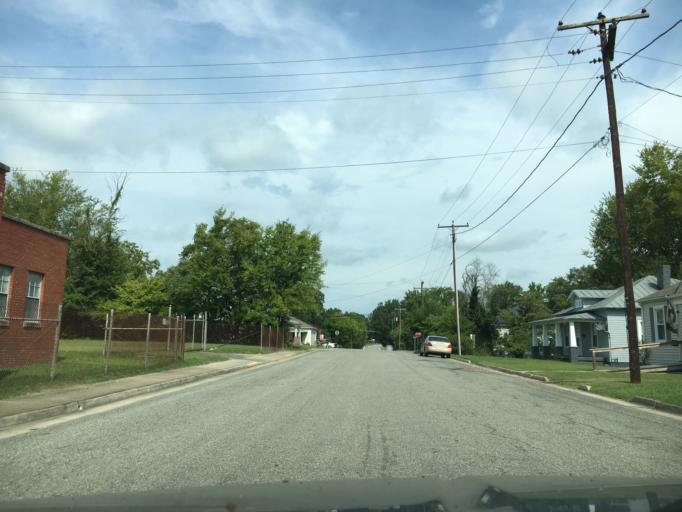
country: US
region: Virginia
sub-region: Halifax County
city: South Boston
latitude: 36.7017
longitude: -78.9072
